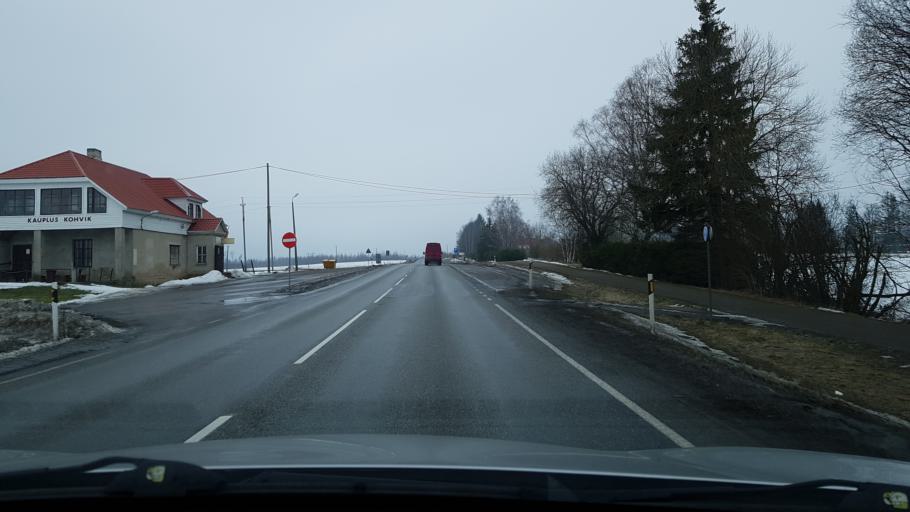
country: EE
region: Valgamaa
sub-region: Valga linn
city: Valga
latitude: 57.9221
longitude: 26.1804
